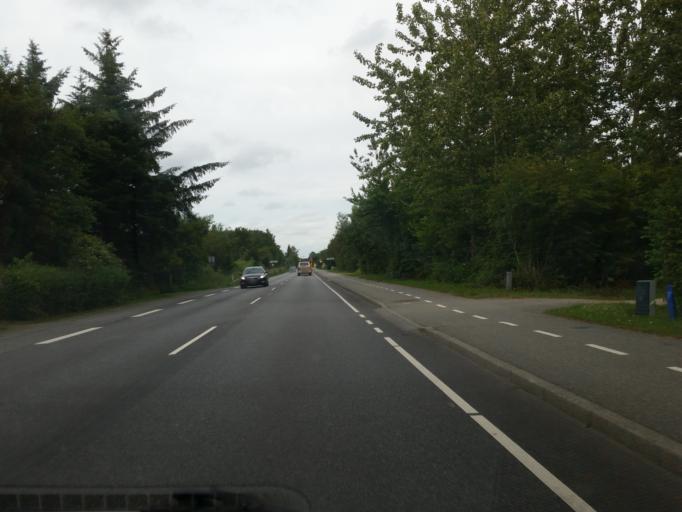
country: DK
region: South Denmark
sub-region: Esbjerg Kommune
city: Ribe
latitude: 55.2684
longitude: 8.7250
